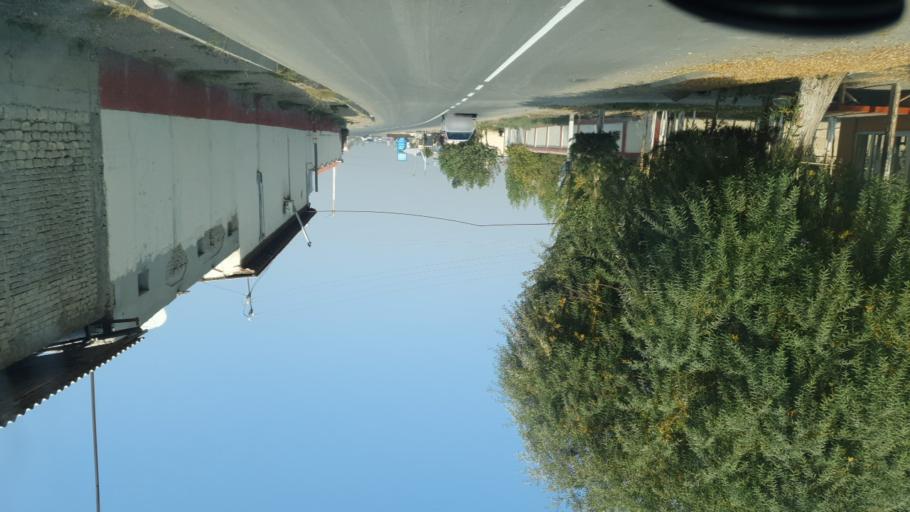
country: UZ
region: Fergana
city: Qo`qon
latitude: 40.5870
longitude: 70.9055
